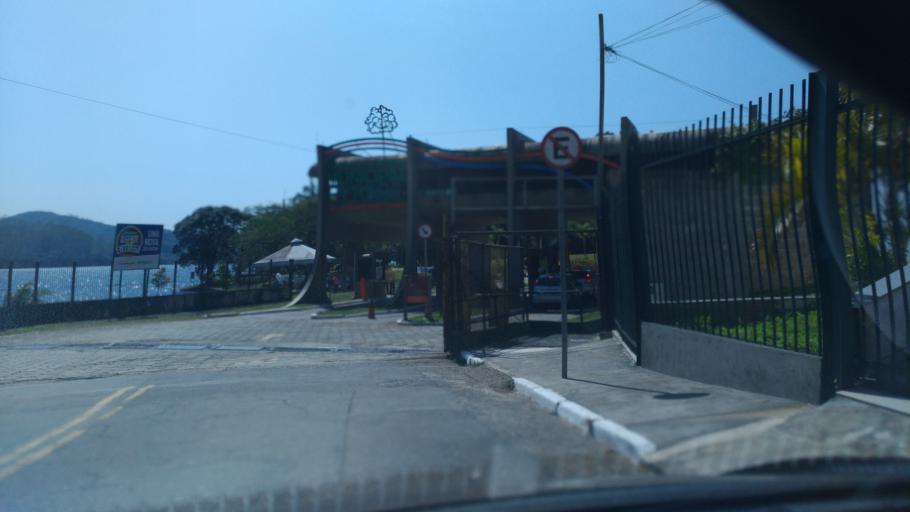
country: BR
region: Sao Paulo
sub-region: Sao Bernardo Do Campo
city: Sao Bernardo do Campo
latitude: -23.7708
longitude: -46.5202
